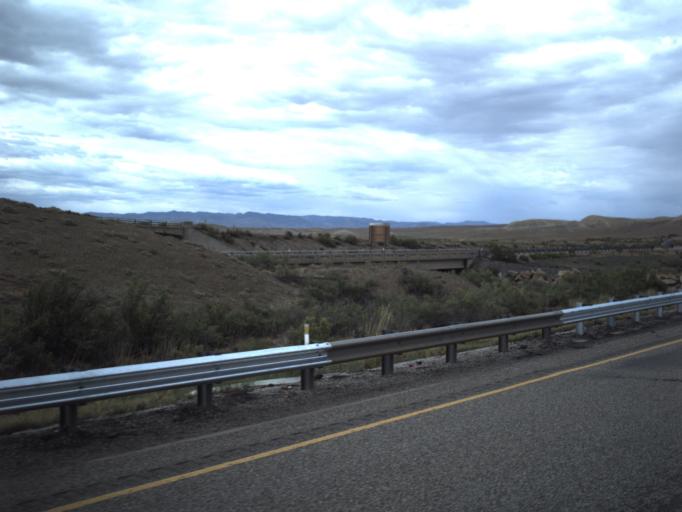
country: US
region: Colorado
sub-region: Mesa County
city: Loma
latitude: 39.1220
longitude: -109.1711
